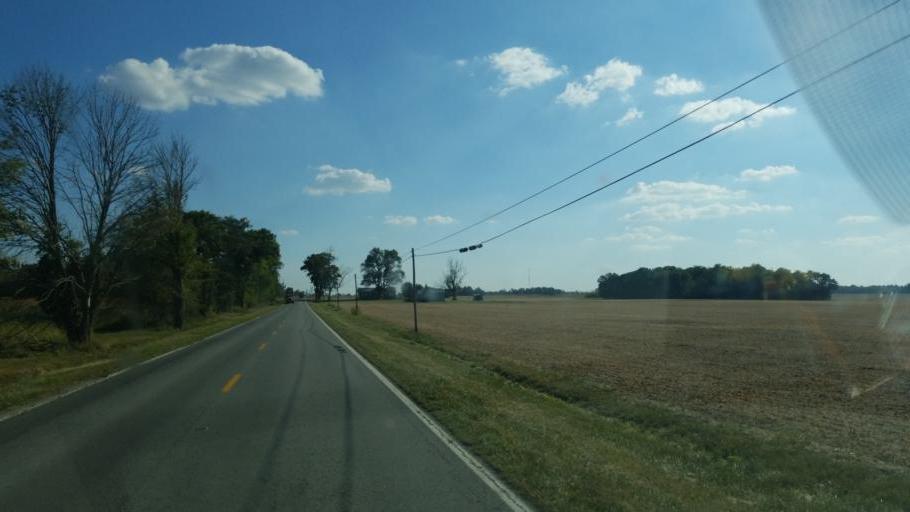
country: US
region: Ohio
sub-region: Hardin County
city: Forest
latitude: 40.6300
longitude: -83.3806
